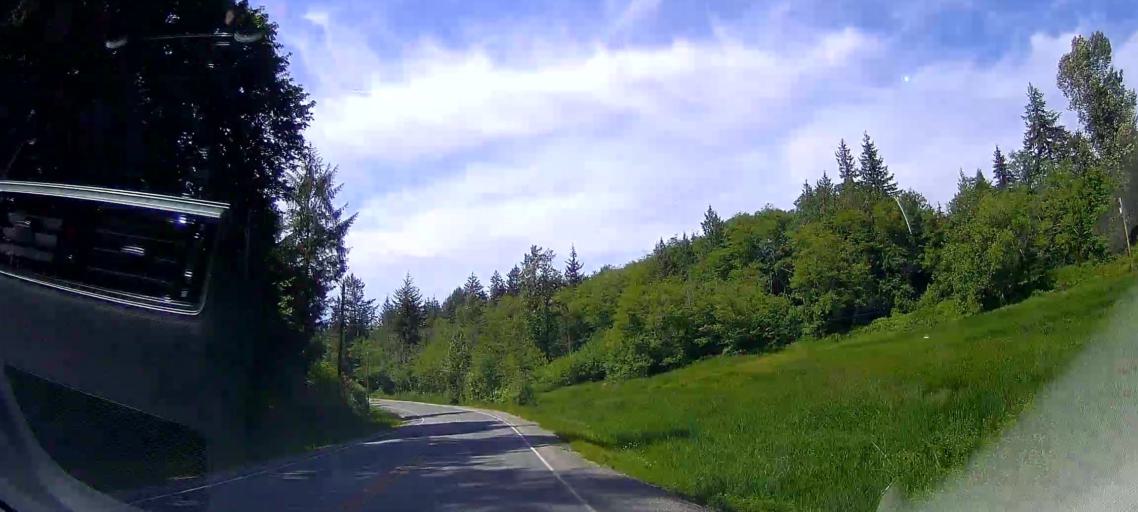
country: US
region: Washington
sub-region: Skagit County
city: Big Lake
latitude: 48.3906
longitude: -122.2560
